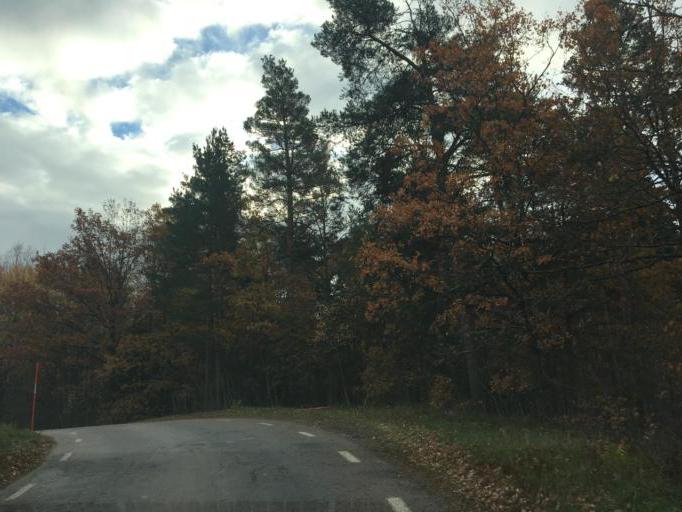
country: SE
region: Vaestmanland
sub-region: Vasteras
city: Vasteras
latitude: 59.5660
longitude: 16.4252
